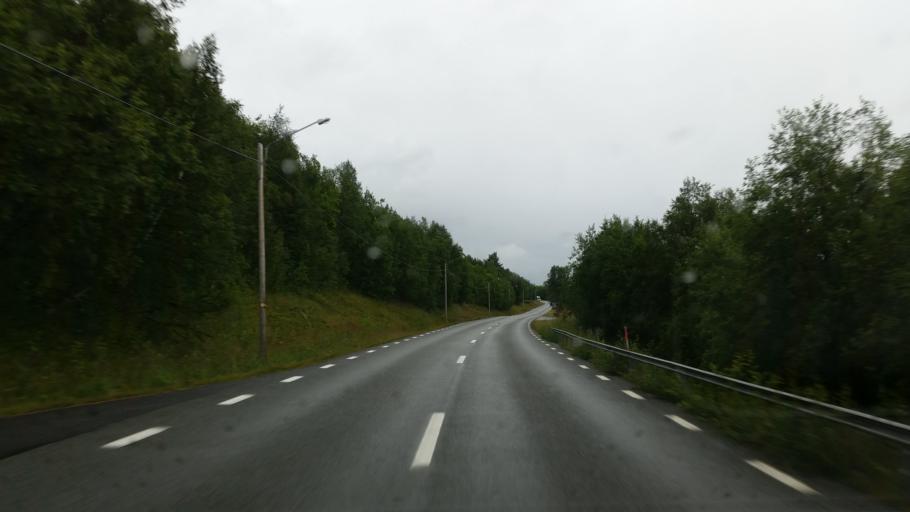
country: NO
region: Nordland
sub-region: Rana
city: Mo i Rana
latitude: 65.8712
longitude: 15.0125
